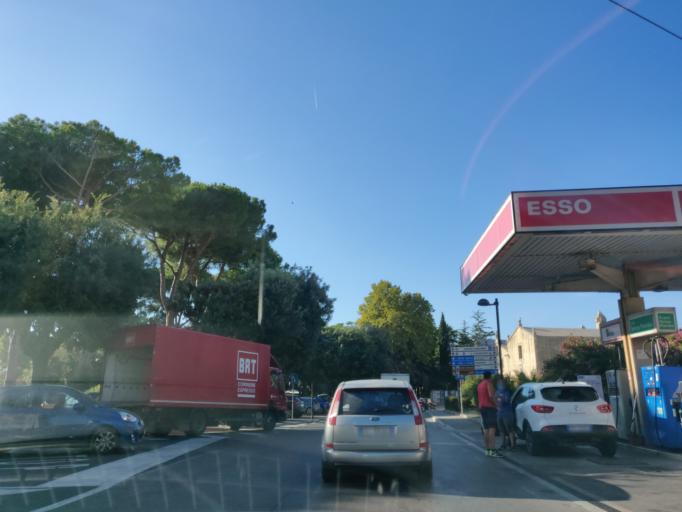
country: IT
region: Tuscany
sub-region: Provincia di Grosseto
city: Orbetello
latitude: 42.4394
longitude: 11.2139
